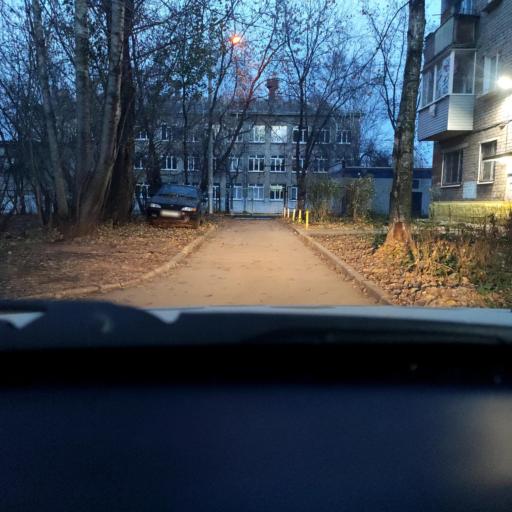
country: RU
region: Perm
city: Perm
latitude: 57.9817
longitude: 56.1843
